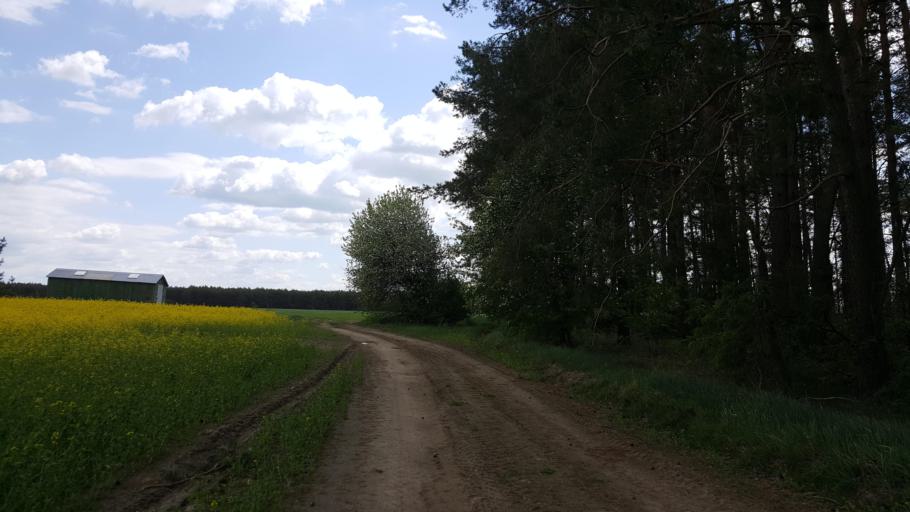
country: BY
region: Brest
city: Kamyanyets
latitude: 52.3867
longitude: 23.9441
